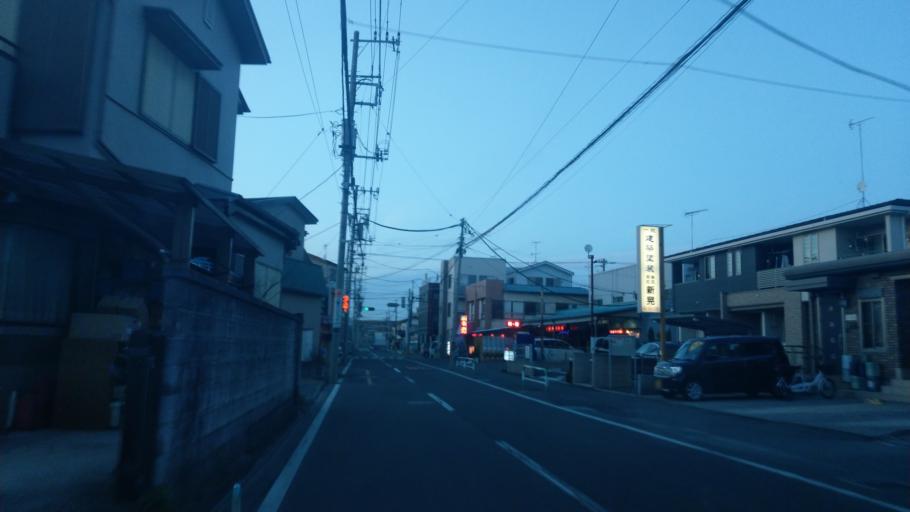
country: JP
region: Saitama
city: Yono
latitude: 35.8753
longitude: 139.6046
